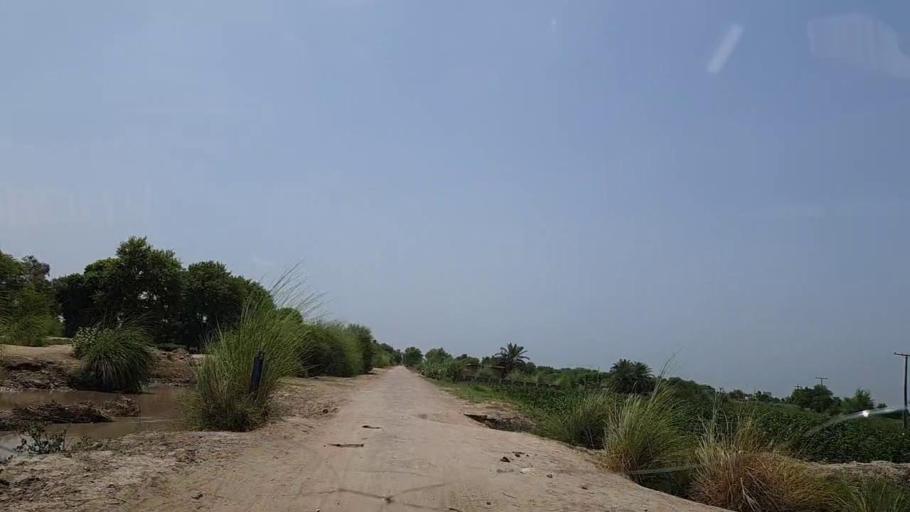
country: PK
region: Sindh
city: Khanpur
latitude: 27.8001
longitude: 69.4823
